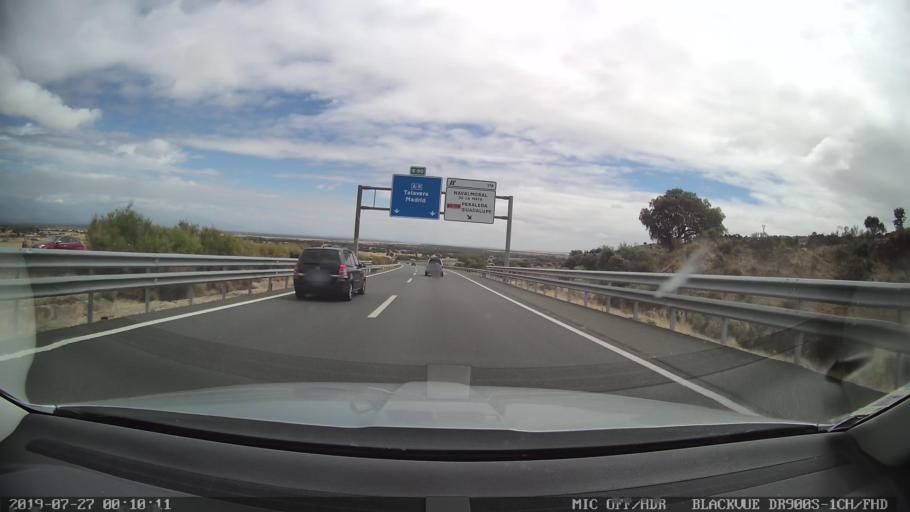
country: ES
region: Extremadura
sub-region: Provincia de Caceres
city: Navalmoral de la Mata
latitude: 39.8880
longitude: -5.5194
